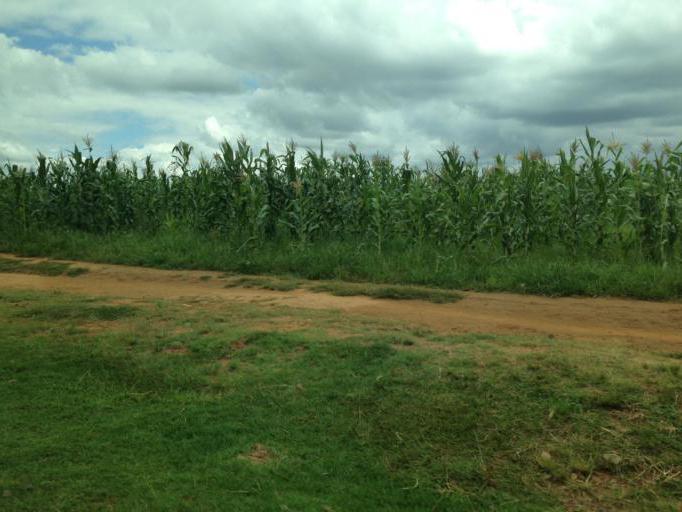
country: LS
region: Leribe
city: Leribe
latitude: -28.9340
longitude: 28.1534
